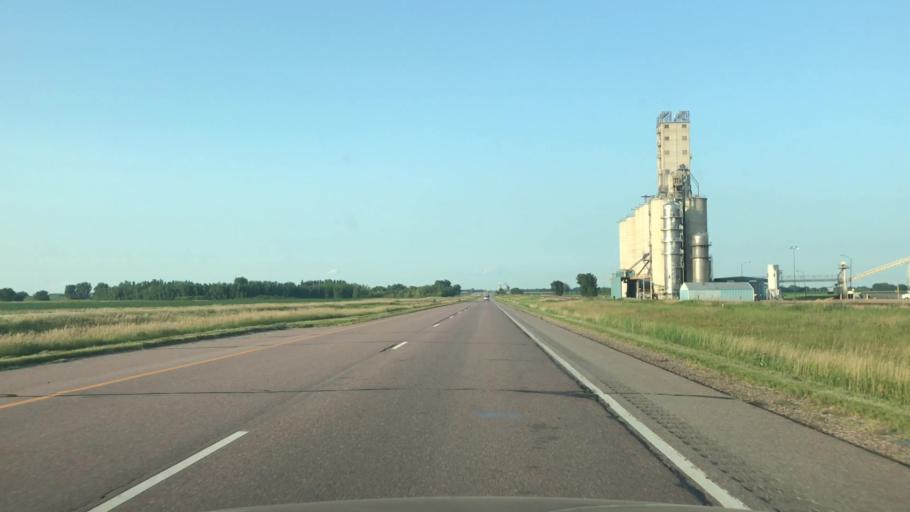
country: US
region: Minnesota
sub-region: Jackson County
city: Lakefield
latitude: 43.7665
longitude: -95.3665
